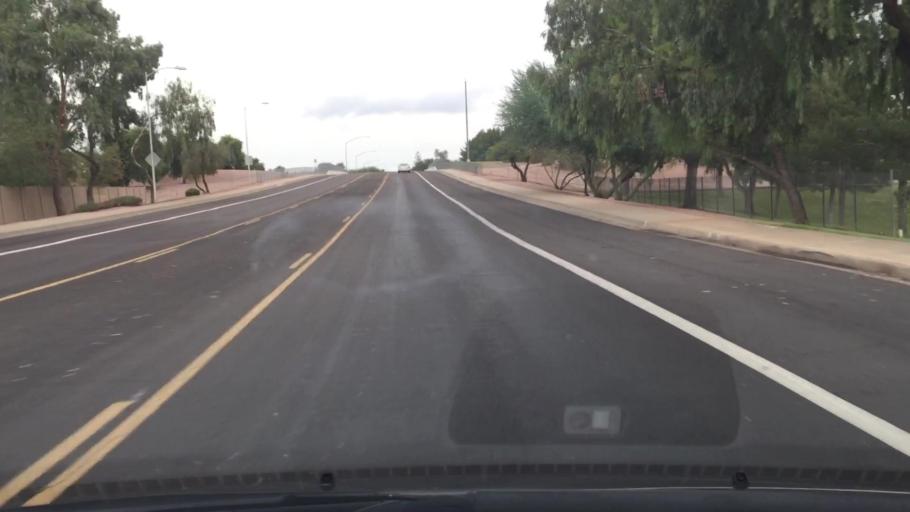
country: US
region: Arizona
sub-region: Maricopa County
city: Gilbert
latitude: 33.3884
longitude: -111.7627
